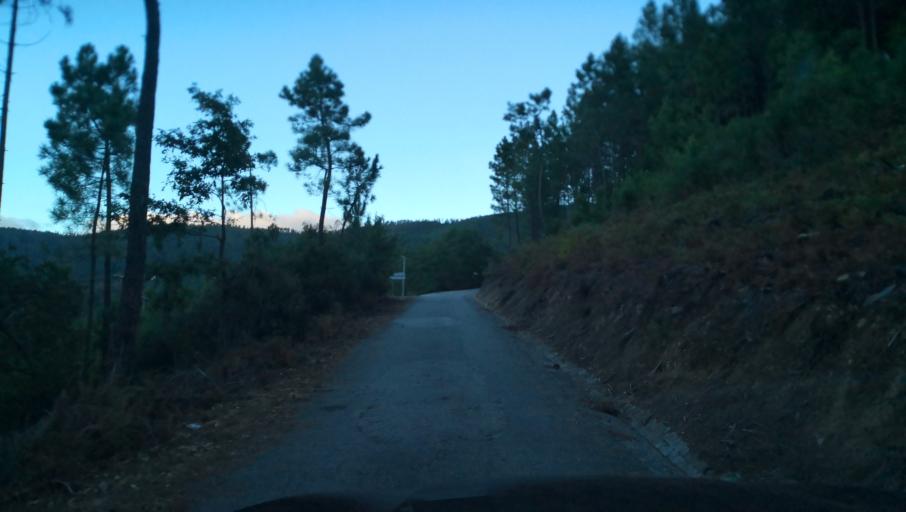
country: PT
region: Vila Real
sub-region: Santa Marta de Penaguiao
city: Santa Marta de Penaguiao
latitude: 41.2586
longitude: -7.8332
